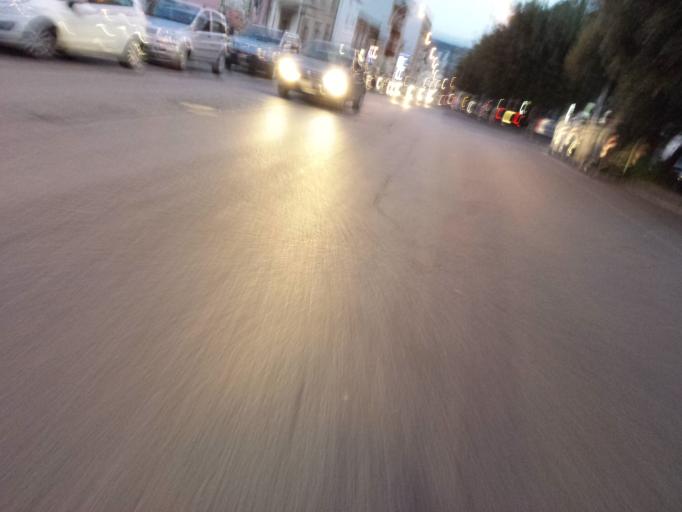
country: IT
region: Molise
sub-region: Provincia di Campobasso
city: Campobasso
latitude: 41.5658
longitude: 14.6720
